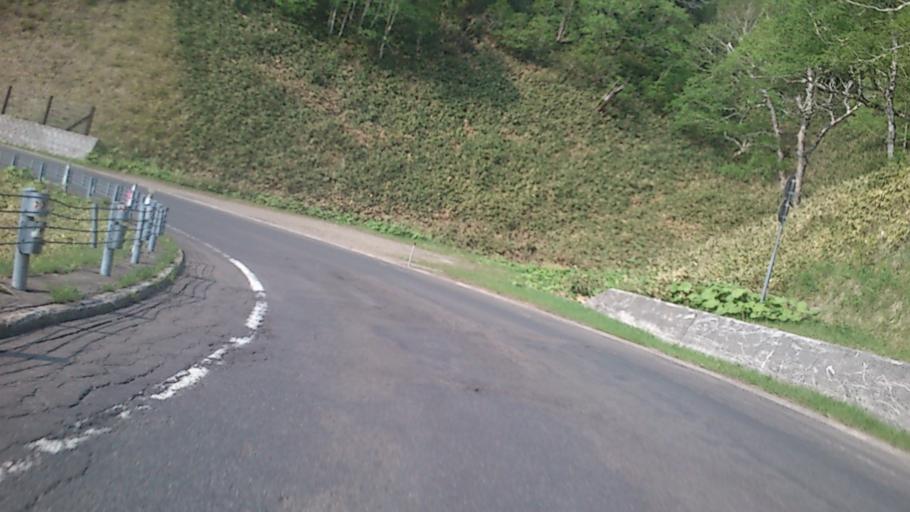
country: JP
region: Hokkaido
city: Bihoro
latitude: 43.4620
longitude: 144.2378
